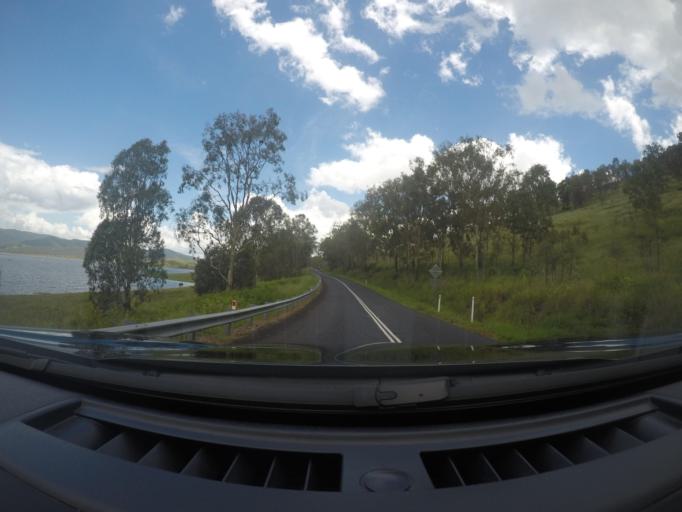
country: AU
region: Queensland
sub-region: Moreton Bay
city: Woodford
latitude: -27.0740
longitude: 152.5649
